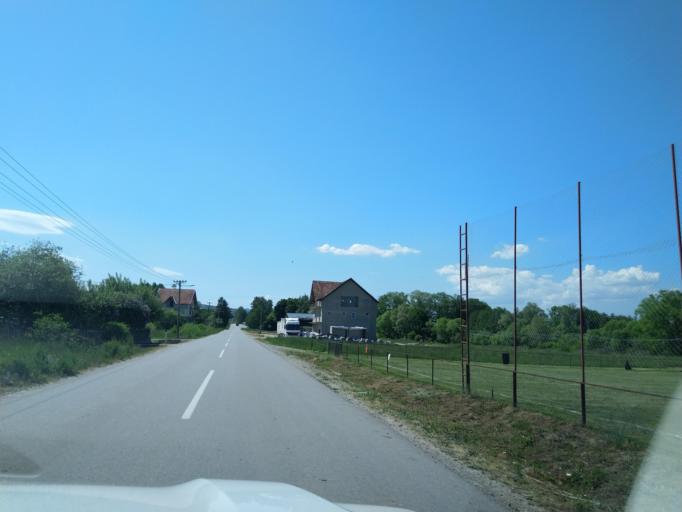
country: RS
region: Central Serbia
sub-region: Zlatiborski Okrug
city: Pozega
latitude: 43.8558
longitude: 19.9832
